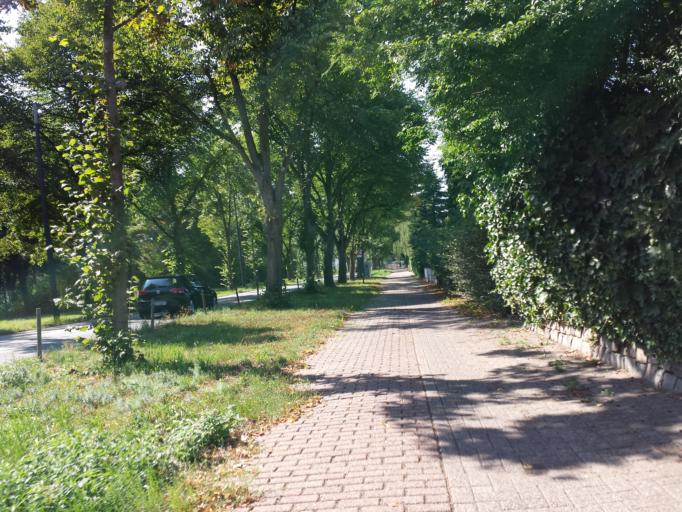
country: DE
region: Bremen
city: Bremen
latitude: 53.0508
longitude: 8.8404
